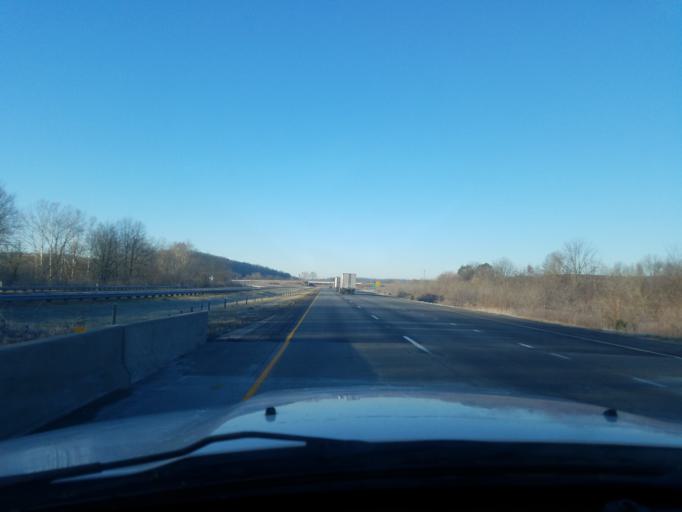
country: US
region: Indiana
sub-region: Dubois County
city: Ferdinand
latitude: 38.2282
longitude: -86.6943
